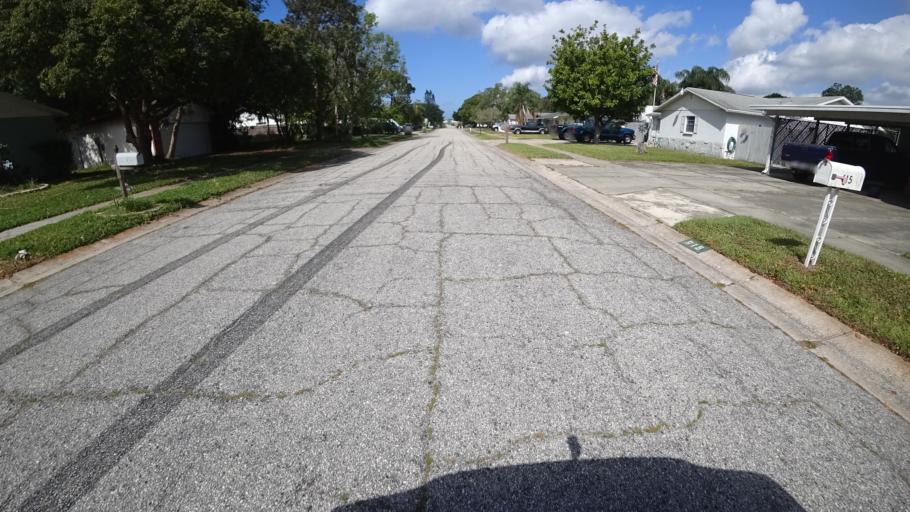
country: US
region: Florida
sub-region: Manatee County
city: Whitfield
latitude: 27.4246
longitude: -82.5691
